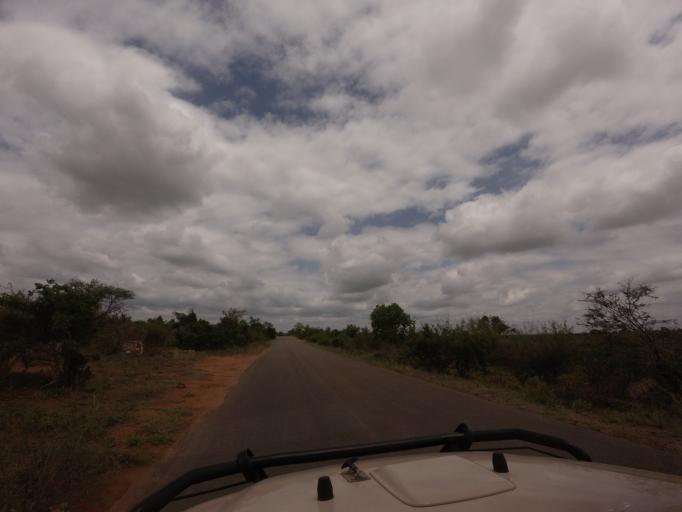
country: ZA
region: Mpumalanga
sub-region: Ehlanzeni District
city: Komatipoort
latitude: -25.1014
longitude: 31.8885
